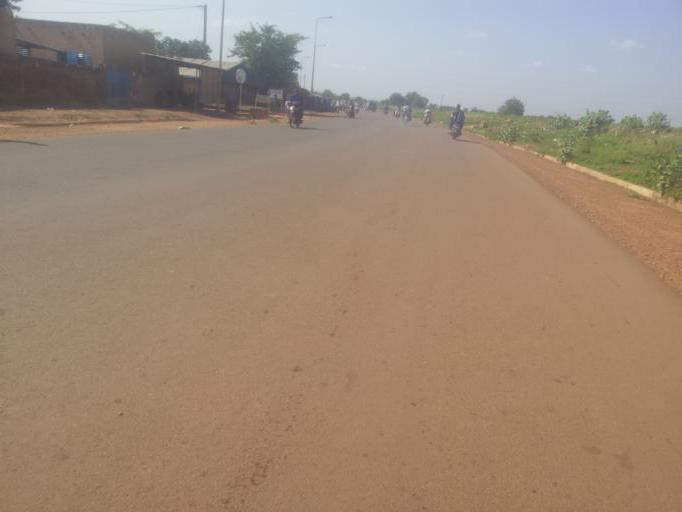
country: BF
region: Centre
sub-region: Kadiogo Province
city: Ouagadougou
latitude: 12.3723
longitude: -1.5685
